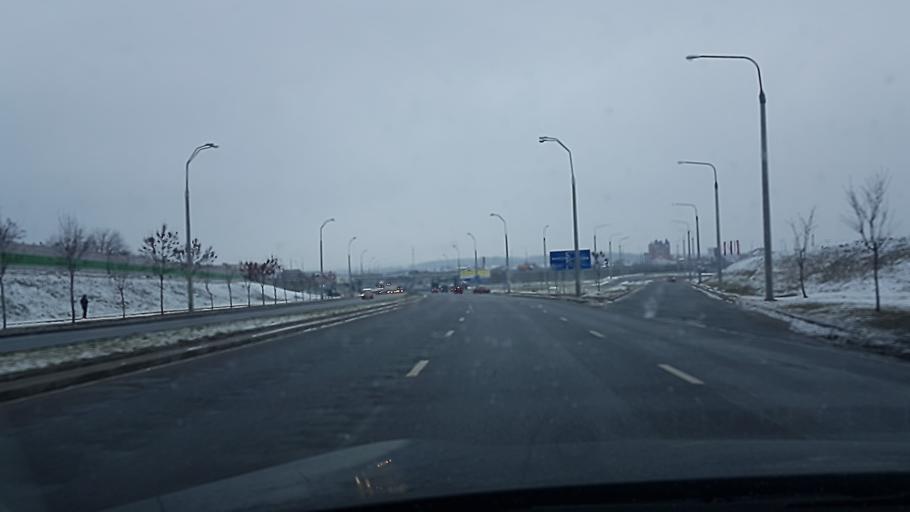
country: BY
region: Minsk
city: Bal'shavik
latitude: 53.9662
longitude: 27.5386
